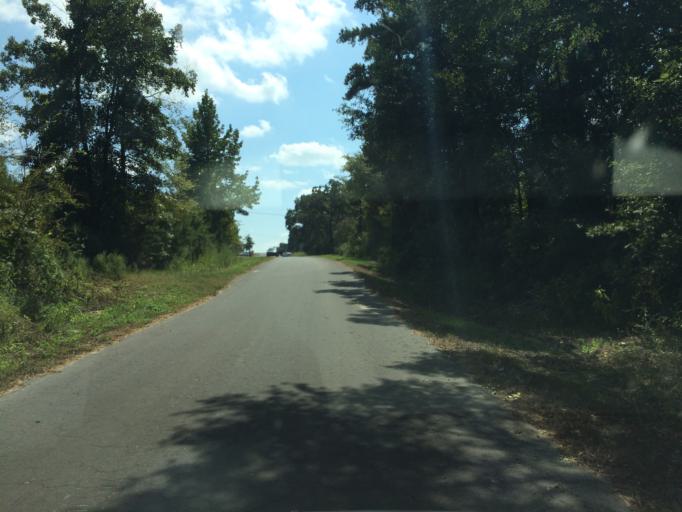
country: US
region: Texas
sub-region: Wood County
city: Hawkins
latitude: 32.7329
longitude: -95.1971
